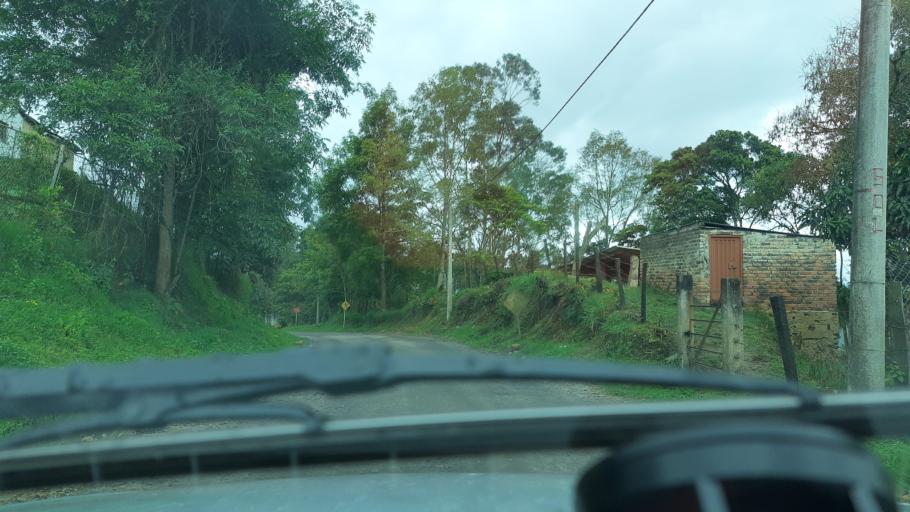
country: CO
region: Boyaca
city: Chinavita
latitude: 5.1692
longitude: -73.3710
